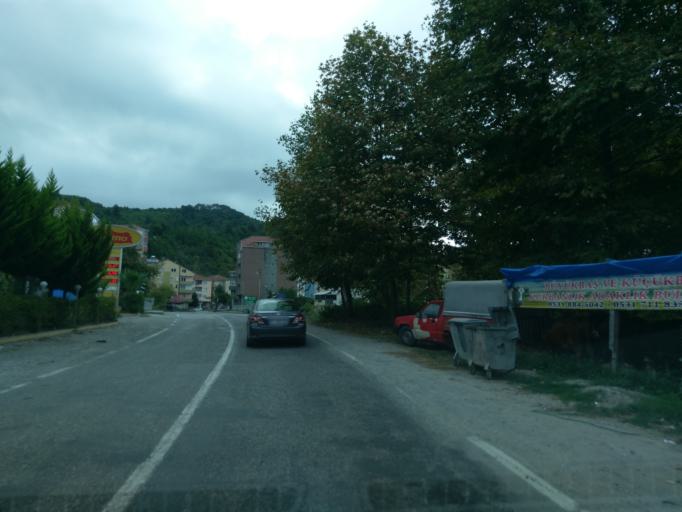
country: TR
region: Sinop
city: Helaldi
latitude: 41.9465
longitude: 34.3936
